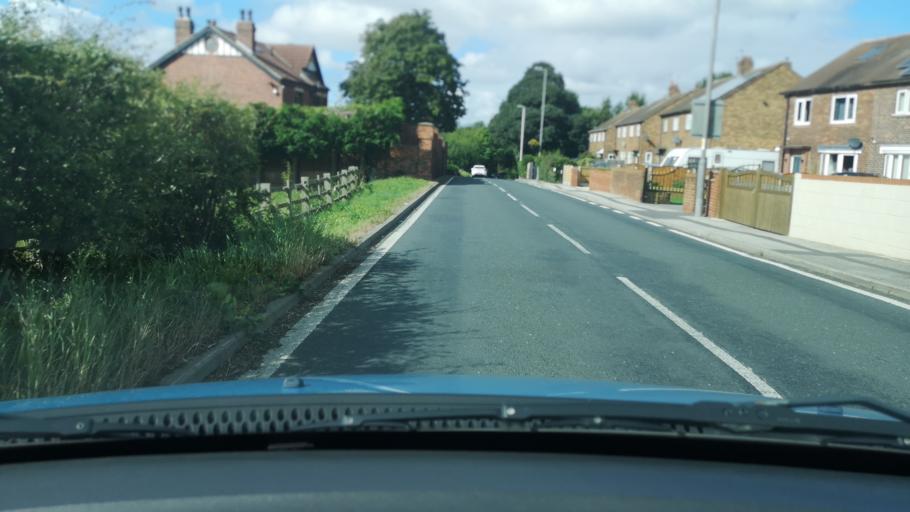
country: GB
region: England
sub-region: City and Borough of Wakefield
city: Featherstone
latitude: 53.6932
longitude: -1.3634
